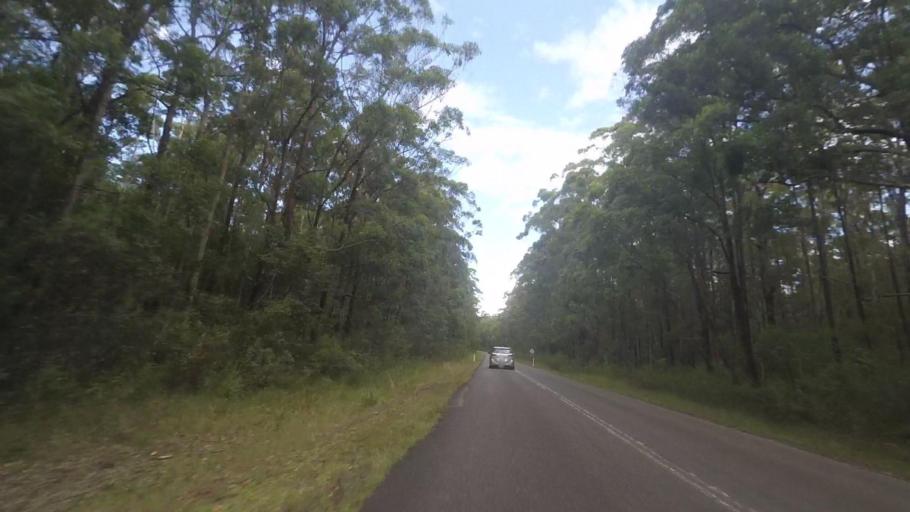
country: AU
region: New South Wales
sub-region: Great Lakes
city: Bulahdelah
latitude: -32.3985
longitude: 152.2547
